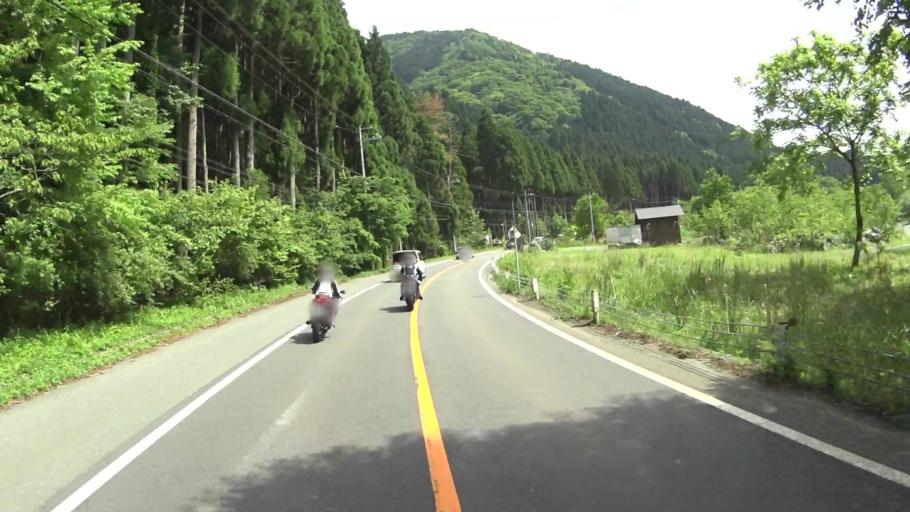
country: JP
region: Shiga Prefecture
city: Kitahama
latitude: 35.2886
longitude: 135.8845
